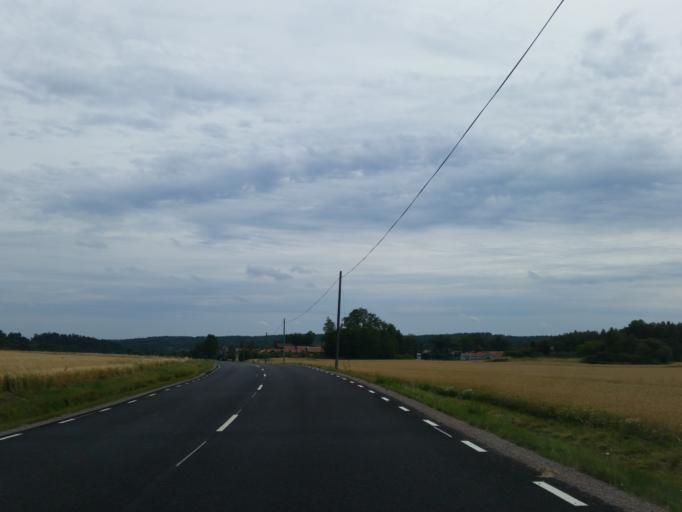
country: SE
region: Soedermanland
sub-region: Strangnas Kommun
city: Mariefred
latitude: 59.2574
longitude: 17.1742
